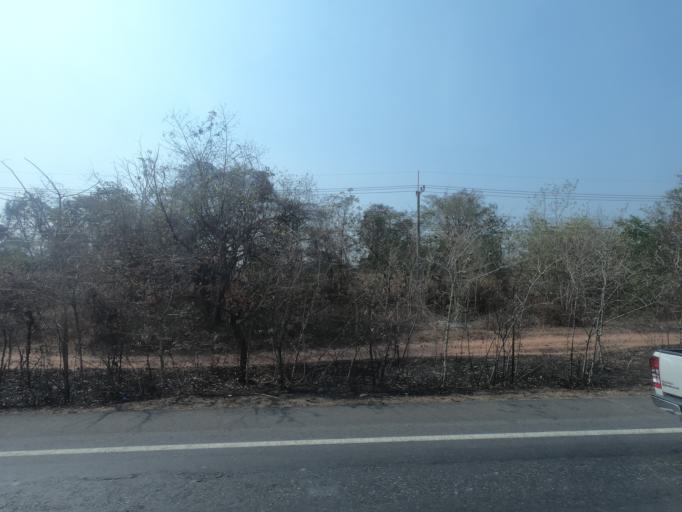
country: TH
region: Nakhon Ratchasima
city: Bua Lai
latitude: 15.6708
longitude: 102.5752
